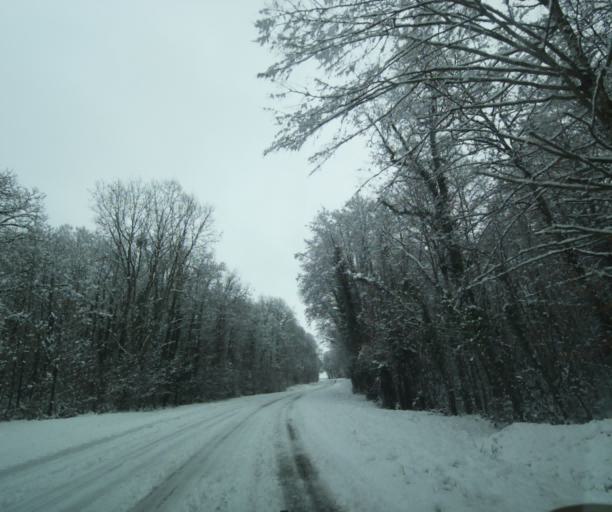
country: FR
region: Champagne-Ardenne
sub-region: Departement de la Haute-Marne
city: Montier-en-Der
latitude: 48.5411
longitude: 4.8062
